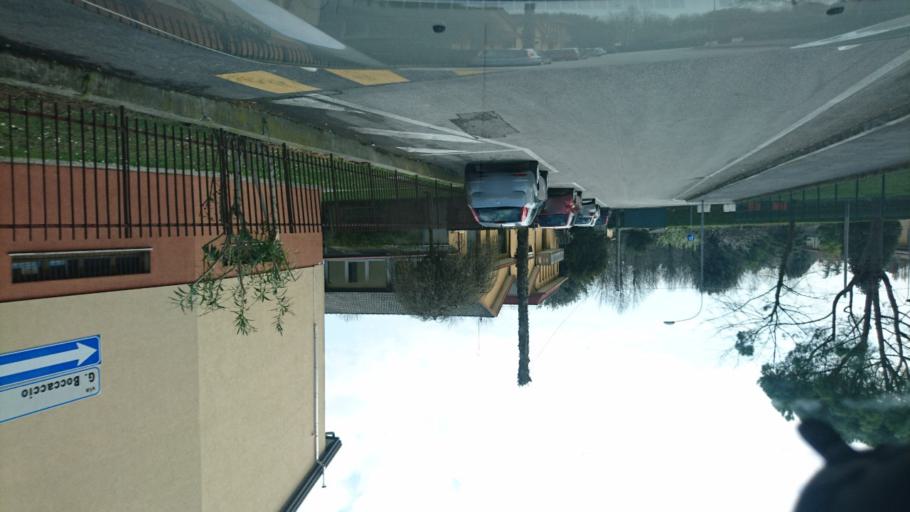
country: IT
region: Veneto
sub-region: Provincia di Padova
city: Noventa
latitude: 45.4103
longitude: 11.9452
